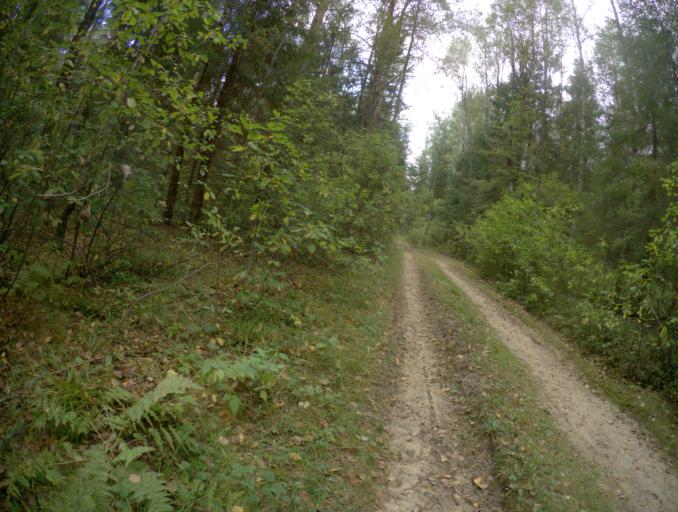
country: RU
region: Vladimir
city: Golovino
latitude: 55.8838
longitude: 40.4360
